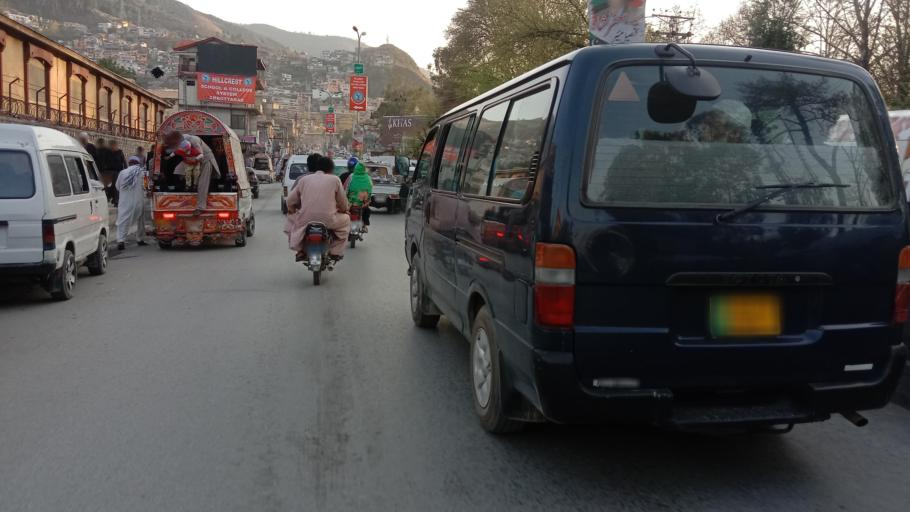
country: PK
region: Khyber Pakhtunkhwa
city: Abbottabad
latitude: 34.1450
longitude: 73.2150
